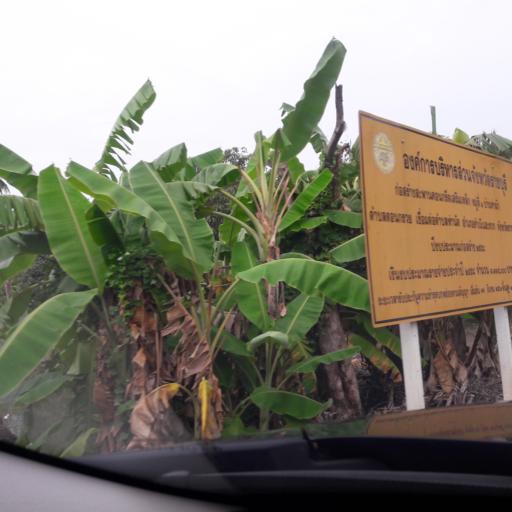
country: TH
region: Ratchaburi
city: Damnoen Saduak
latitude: 13.5599
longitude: 99.9550
